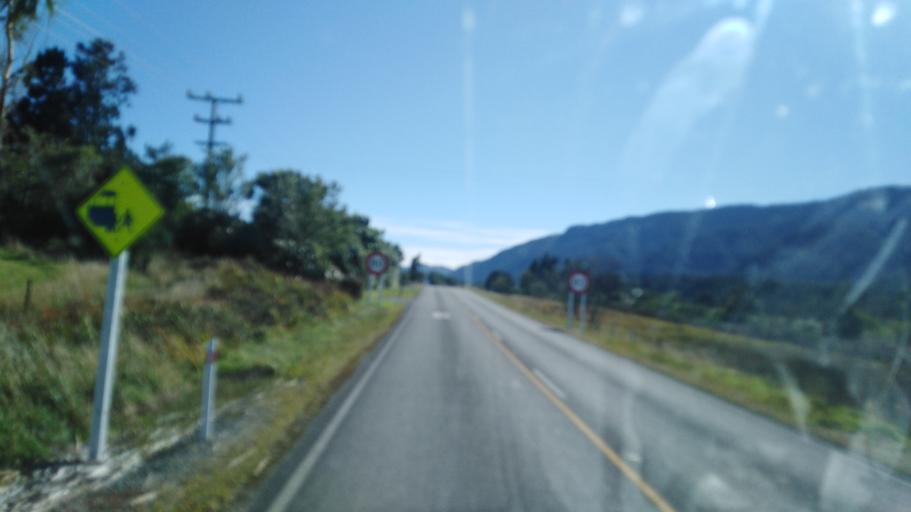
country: NZ
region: West Coast
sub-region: Buller District
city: Westport
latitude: -41.6800
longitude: 171.7935
